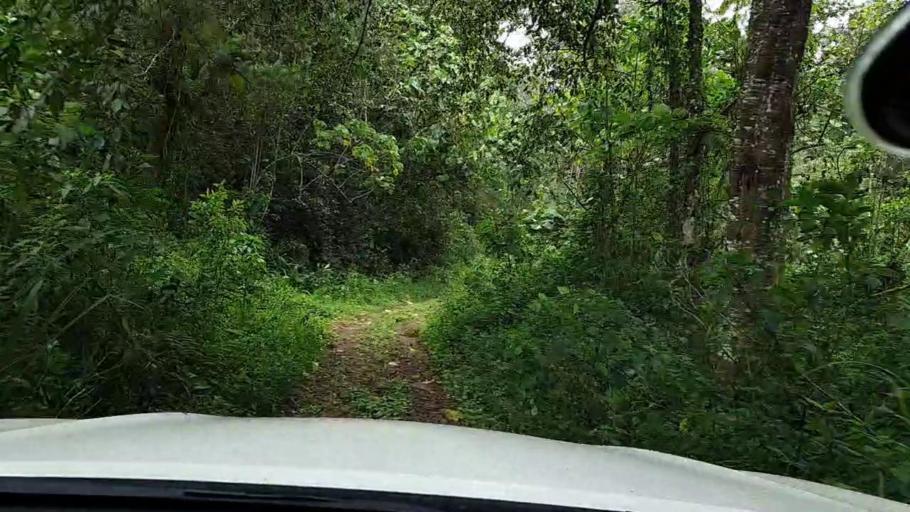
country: RW
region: Western Province
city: Kibuye
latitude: -2.2881
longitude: 29.3051
